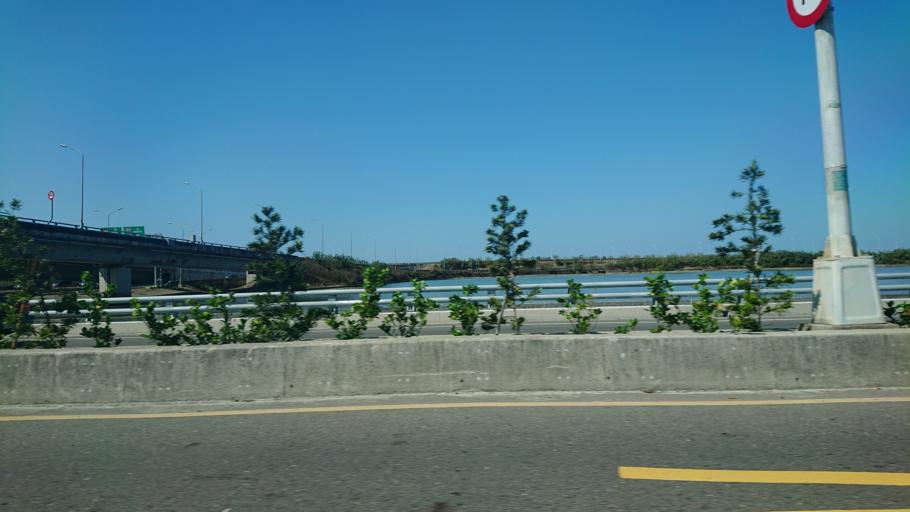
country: TW
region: Taiwan
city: Xinying
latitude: 23.2788
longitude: 120.1303
